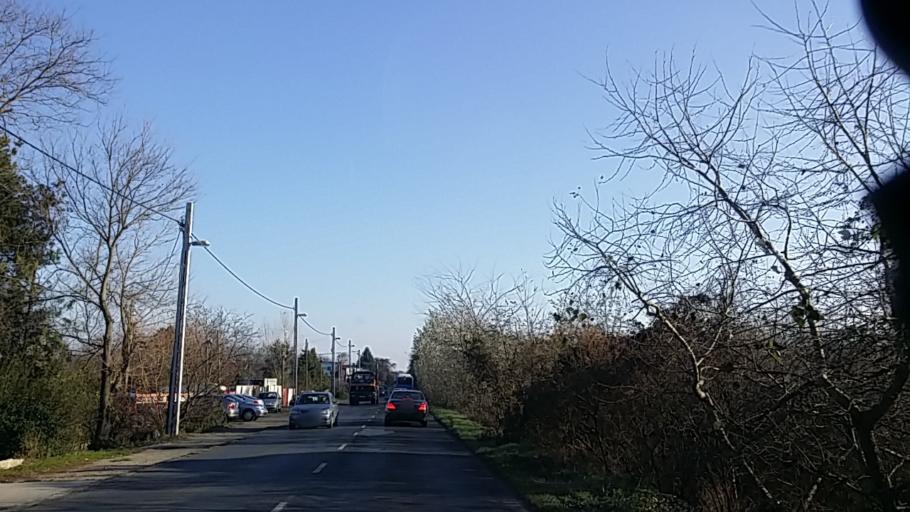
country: HU
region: Budapest
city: Budapest XVIII. keruelet
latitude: 47.4542
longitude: 19.2184
